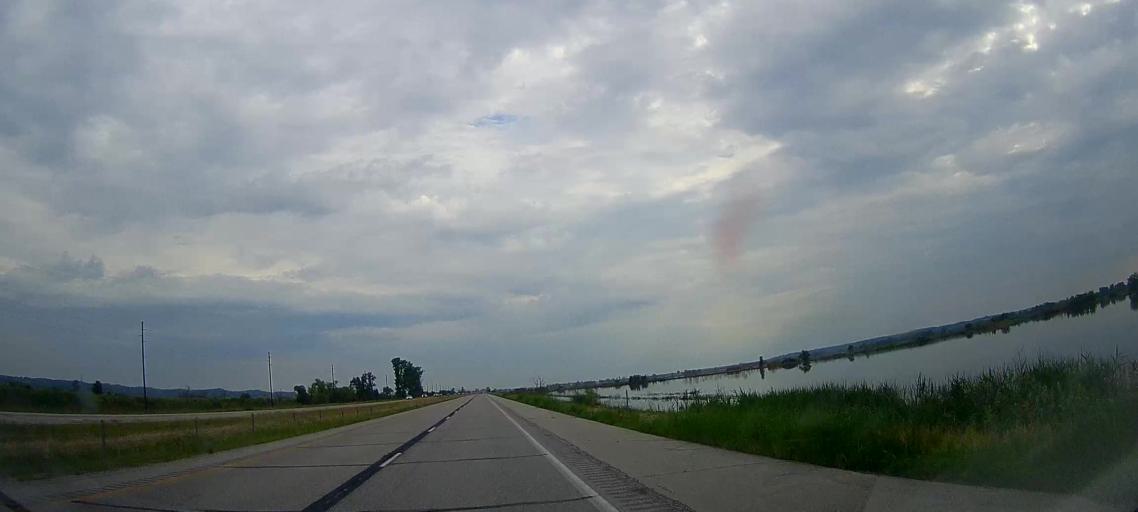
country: US
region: Iowa
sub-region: Harrison County
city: Missouri Valley
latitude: 41.4611
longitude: -95.8998
